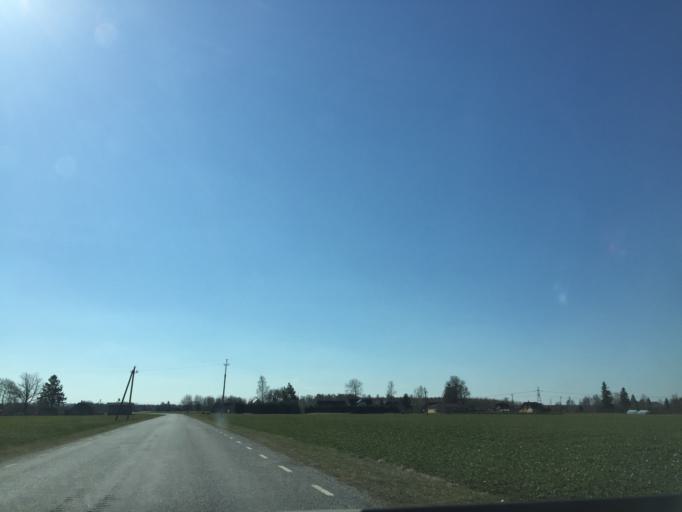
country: EE
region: Tartu
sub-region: Puhja vald
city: Puhja
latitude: 58.3558
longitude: 26.4289
